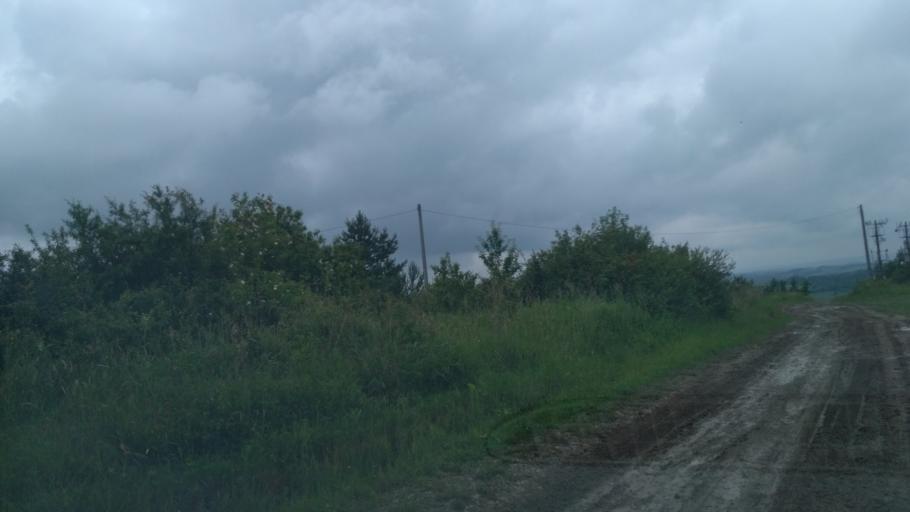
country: PL
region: Subcarpathian Voivodeship
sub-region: Powiat jaroslawski
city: Pruchnik
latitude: 49.8876
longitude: 22.5148
